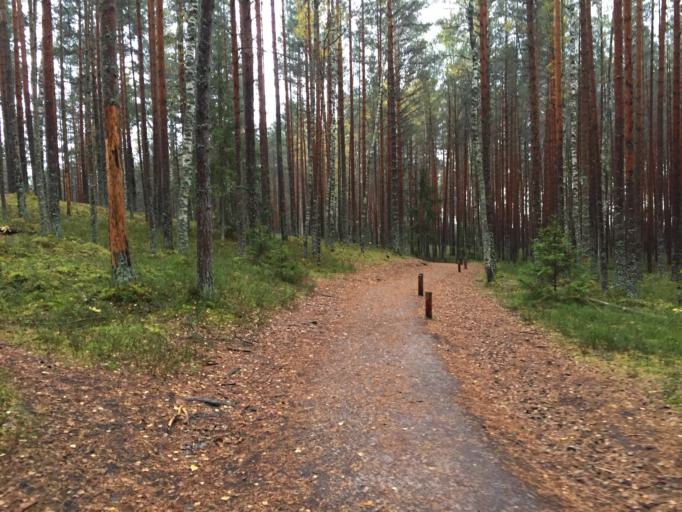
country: LV
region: Engure
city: Smarde
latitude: 56.9122
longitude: 23.4594
